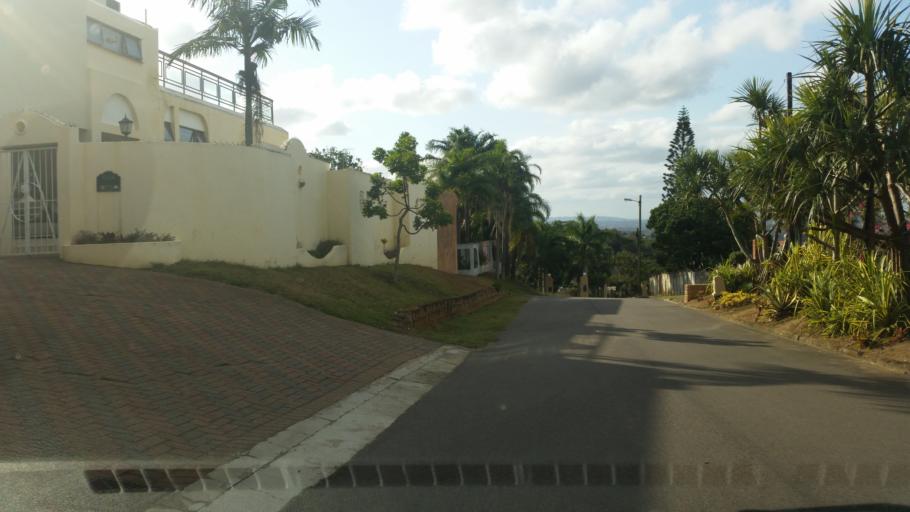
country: ZA
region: KwaZulu-Natal
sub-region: eThekwini Metropolitan Municipality
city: Berea
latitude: -29.8299
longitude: 30.9532
